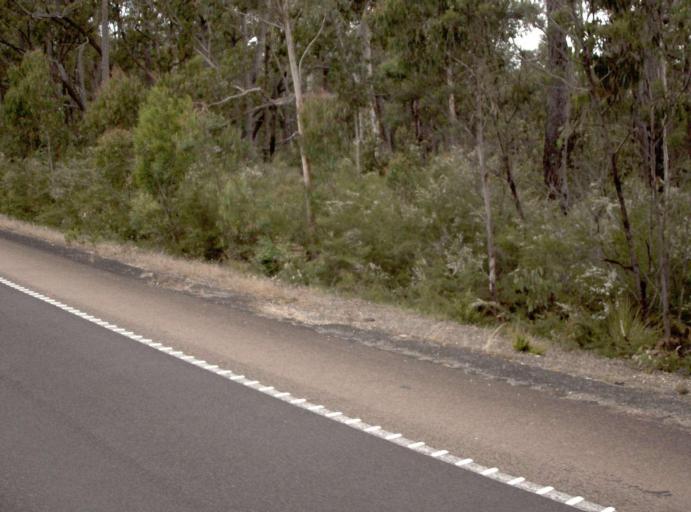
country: AU
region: Victoria
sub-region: East Gippsland
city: Lakes Entrance
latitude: -37.7161
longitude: 147.9612
